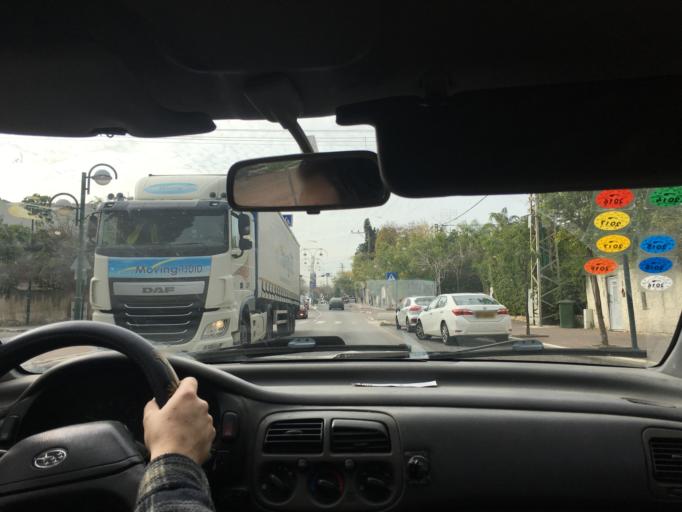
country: IL
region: Tel Aviv
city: Ramat HaSharon
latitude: 32.1356
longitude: 34.8474
